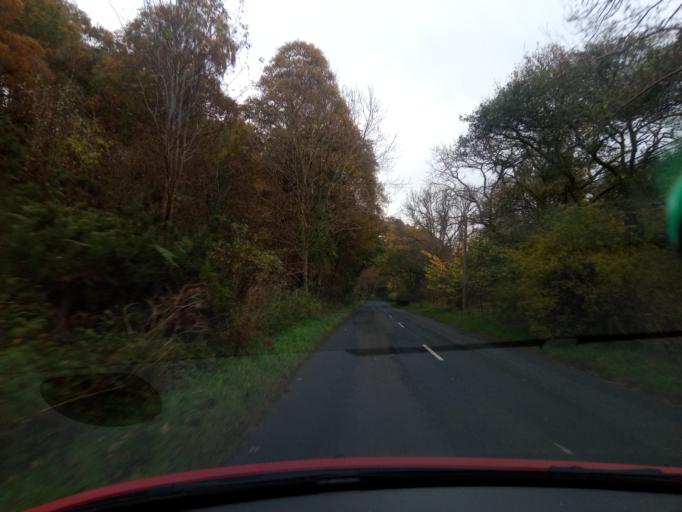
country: GB
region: Scotland
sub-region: The Scottish Borders
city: Galashiels
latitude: 55.6089
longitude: -2.8764
